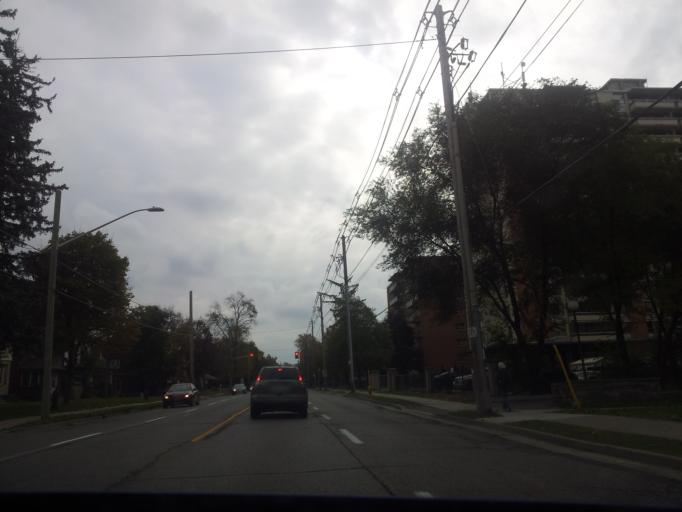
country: CA
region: Ontario
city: London
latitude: 43.0122
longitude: -81.2648
